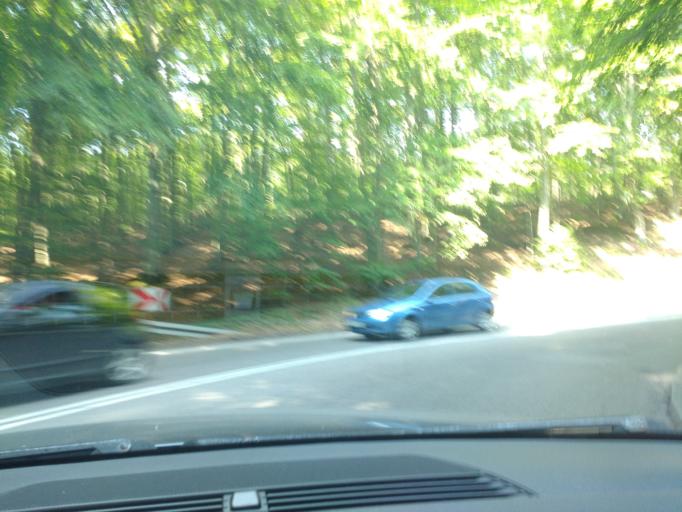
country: PL
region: Pomeranian Voivodeship
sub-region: Gdynia
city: Wielki Kack
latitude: 54.4590
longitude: 18.5076
